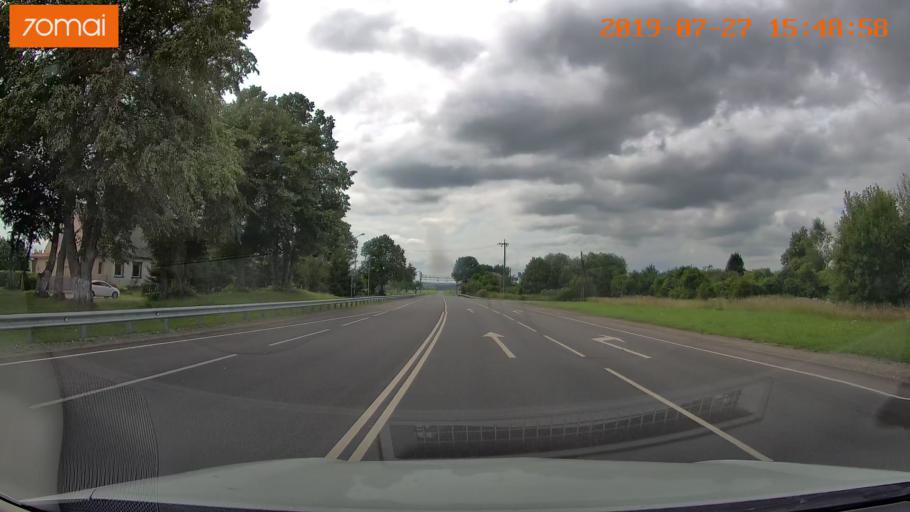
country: RU
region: Kaliningrad
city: Gusev
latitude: 54.6020
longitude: 22.0473
